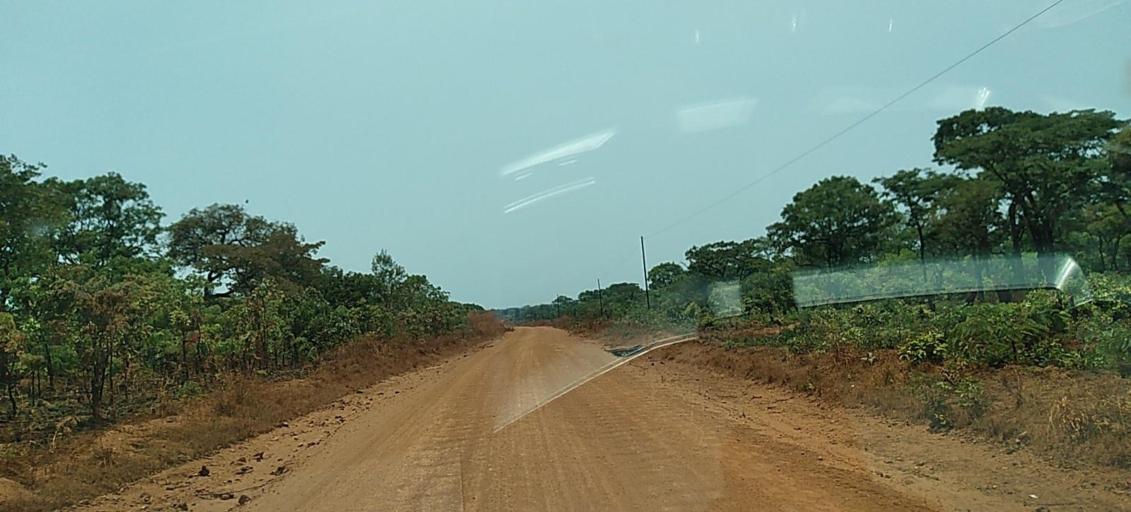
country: CD
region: Katanga
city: Kipushi
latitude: -11.9393
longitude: 26.9499
